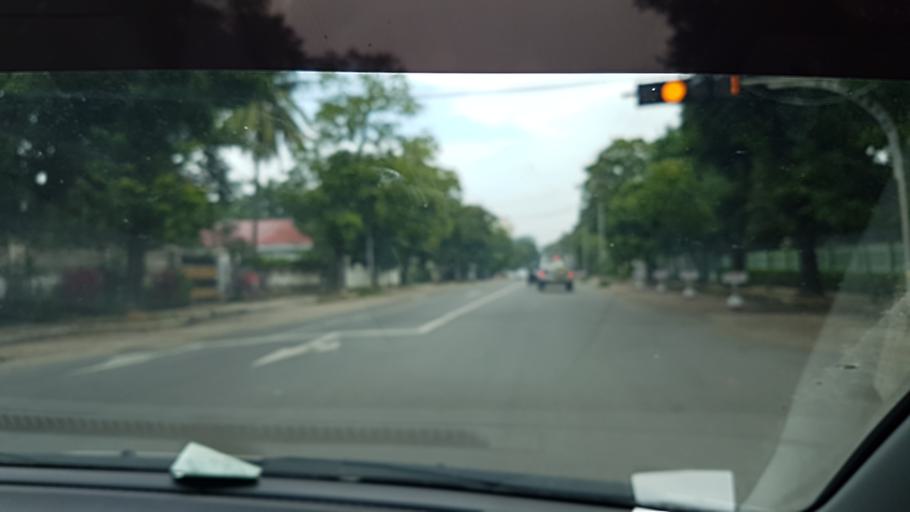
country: MM
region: Yangon
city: Yangon
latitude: 16.7890
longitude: 96.1370
